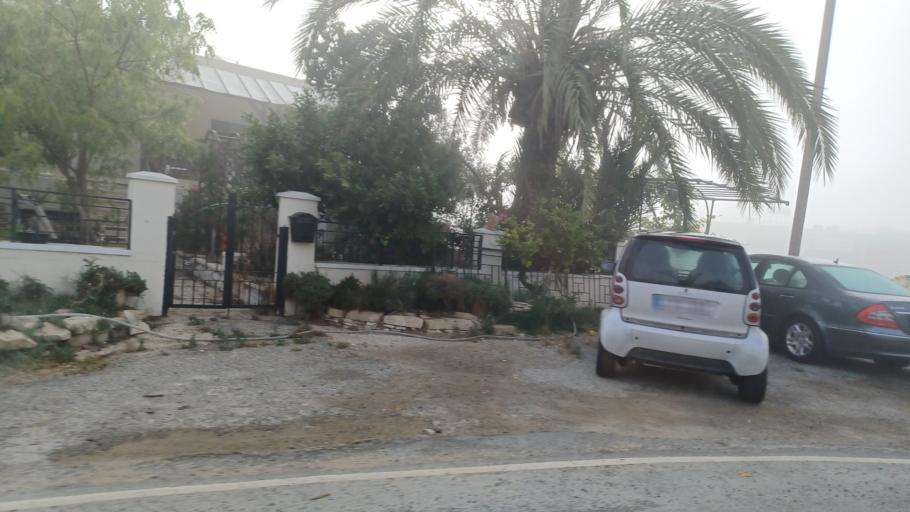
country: CY
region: Ammochostos
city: Acheritou
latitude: 35.0848
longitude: 33.8770
